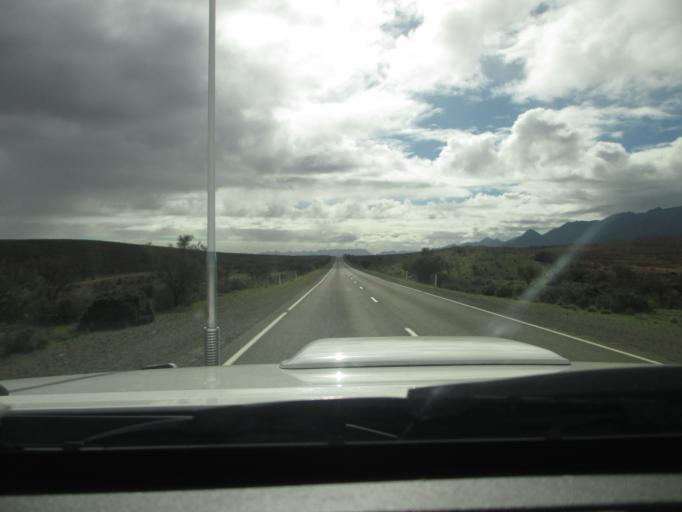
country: AU
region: South Australia
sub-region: Flinders Ranges
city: Quorn
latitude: -31.5817
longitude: 138.4181
